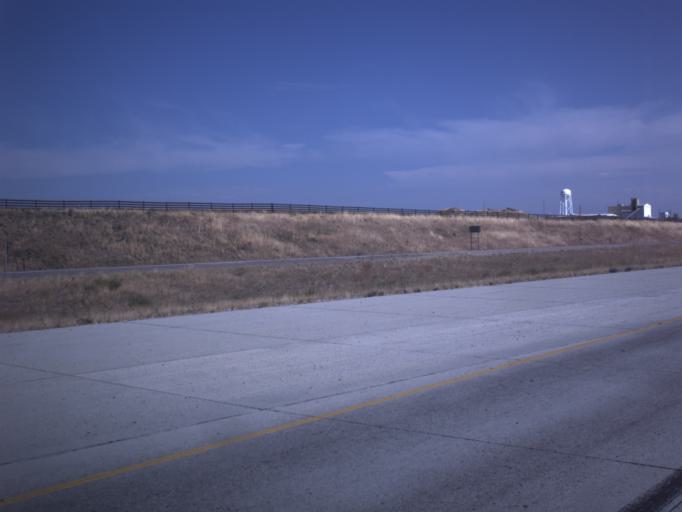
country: US
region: Utah
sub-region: Salt Lake County
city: Oquirrh
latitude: 40.6433
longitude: -112.0448
